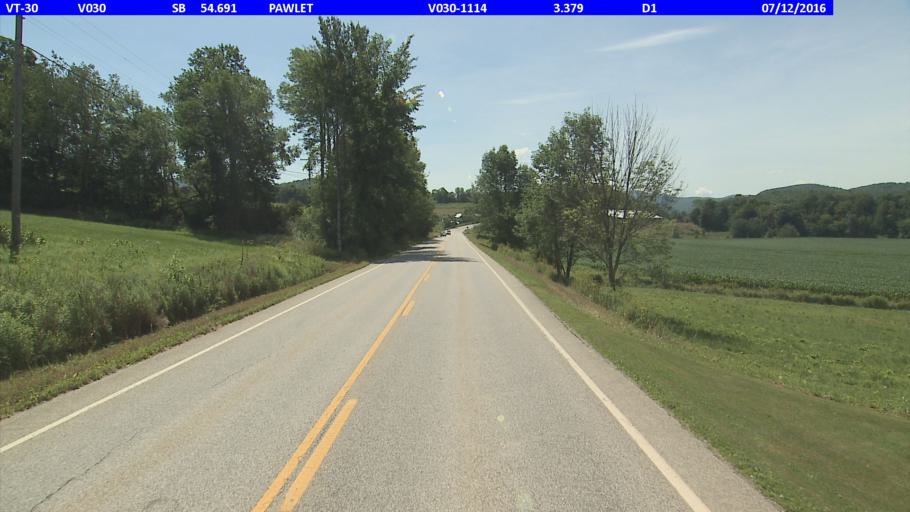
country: US
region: New York
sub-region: Washington County
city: Granville
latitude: 43.3559
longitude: -73.1839
